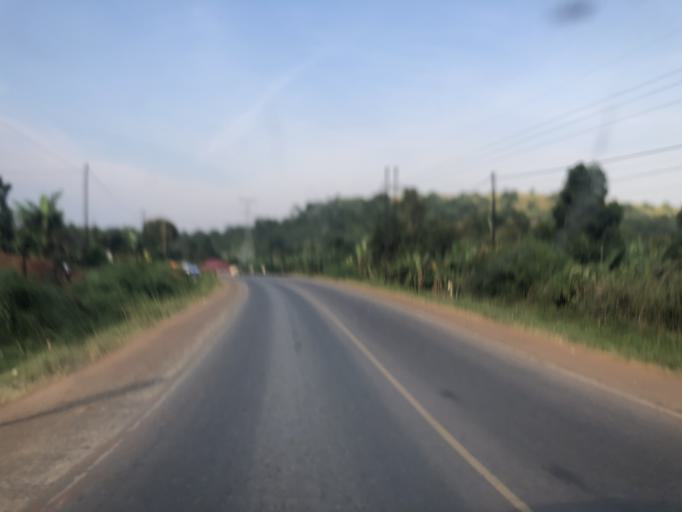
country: UG
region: Central Region
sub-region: Mpigi District
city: Mpigi
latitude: 0.1732
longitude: 32.2721
